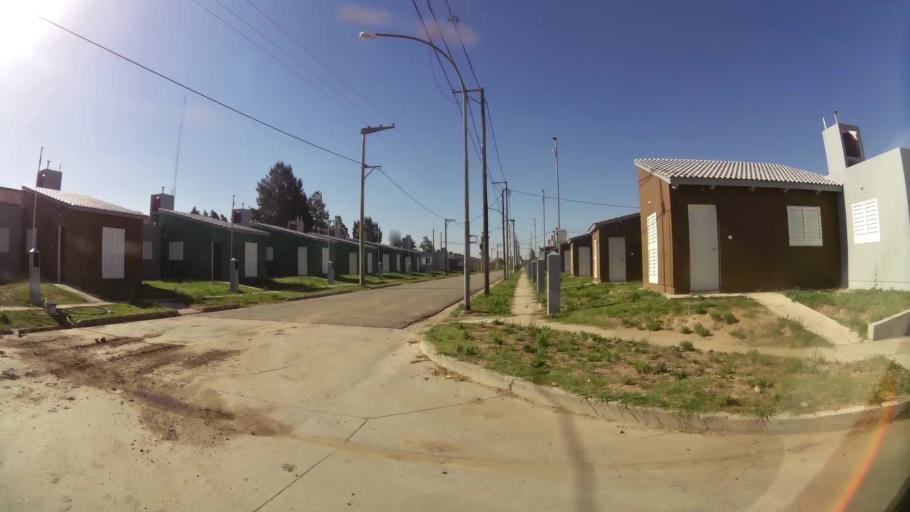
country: AR
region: Cordoba
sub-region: Departamento de Capital
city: Cordoba
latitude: -31.3568
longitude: -64.1940
